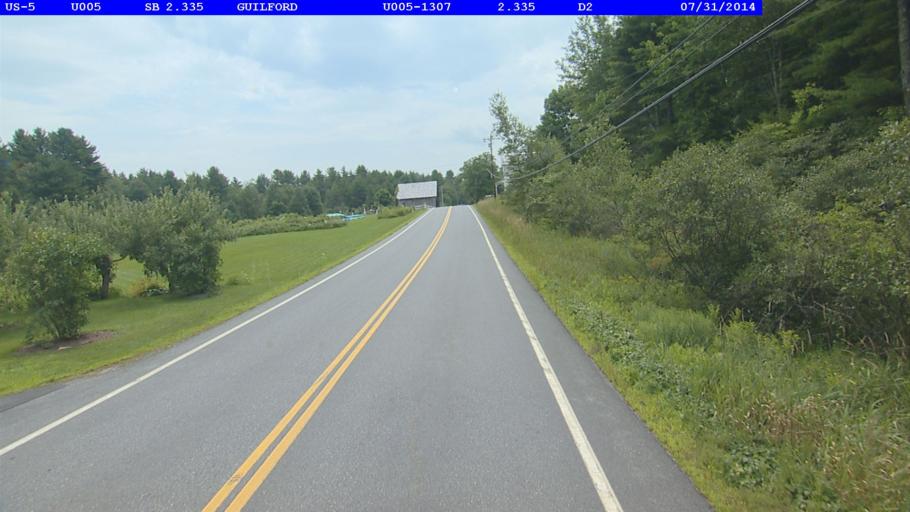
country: US
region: New Hampshire
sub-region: Cheshire County
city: Hinsdale
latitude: 42.7632
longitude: -72.5688
